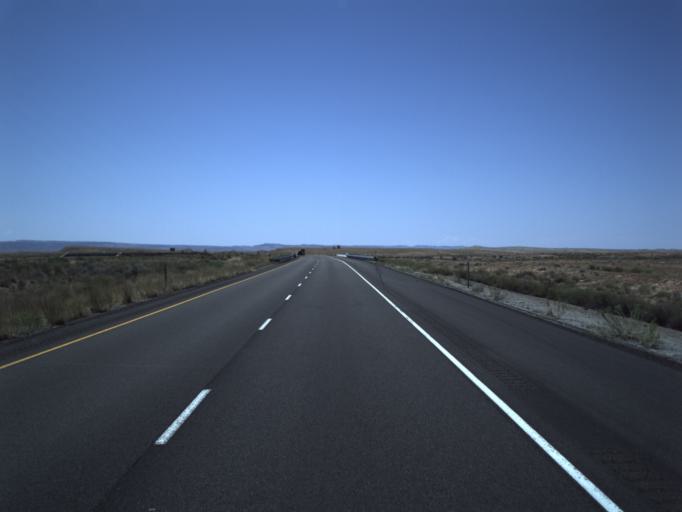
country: US
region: Colorado
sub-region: Mesa County
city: Loma
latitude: 39.0392
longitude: -109.2815
